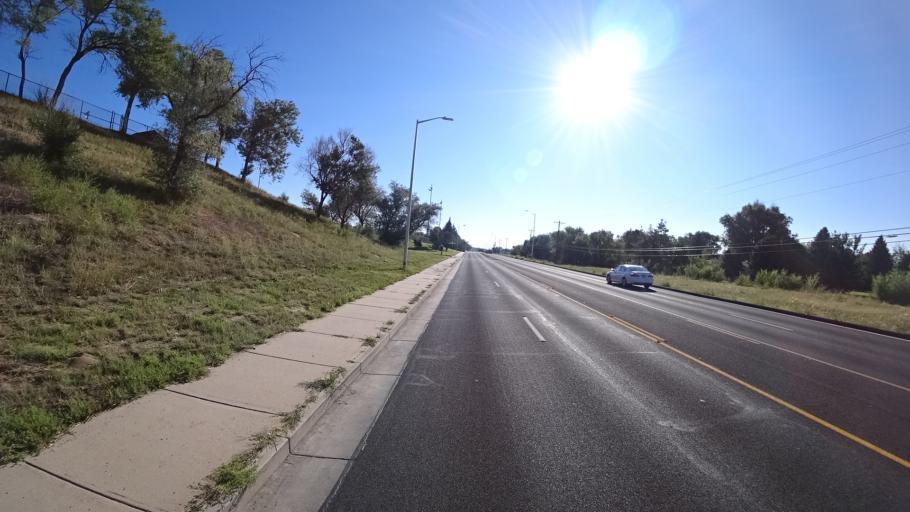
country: US
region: Colorado
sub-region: El Paso County
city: Colorado Springs
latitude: 38.8594
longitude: -104.7804
